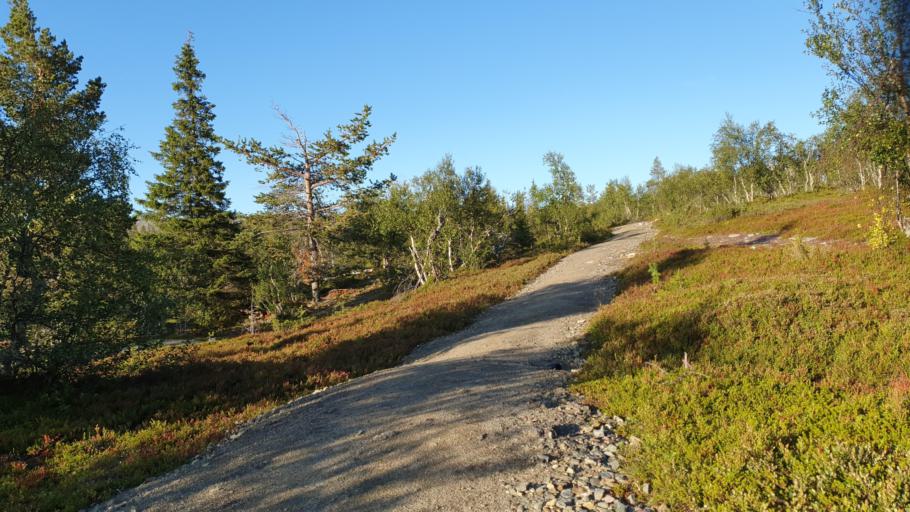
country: FI
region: Lapland
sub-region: Tunturi-Lappi
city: Kolari
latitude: 67.5828
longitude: 24.2347
